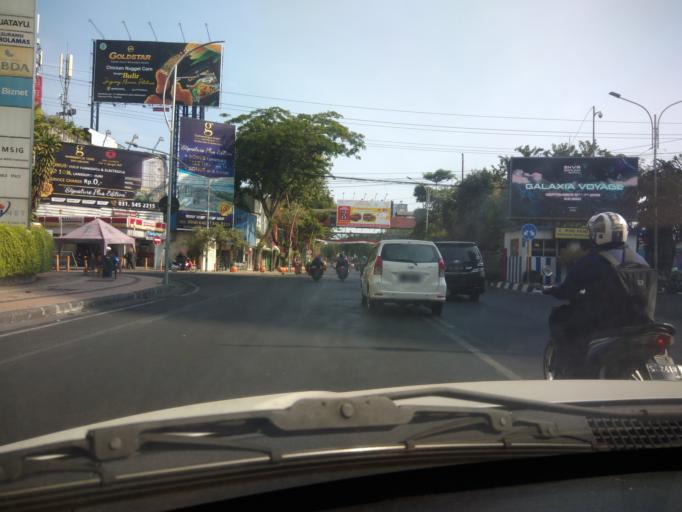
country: ID
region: East Java
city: Gubengairlangga
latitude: -7.2729
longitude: 112.7424
